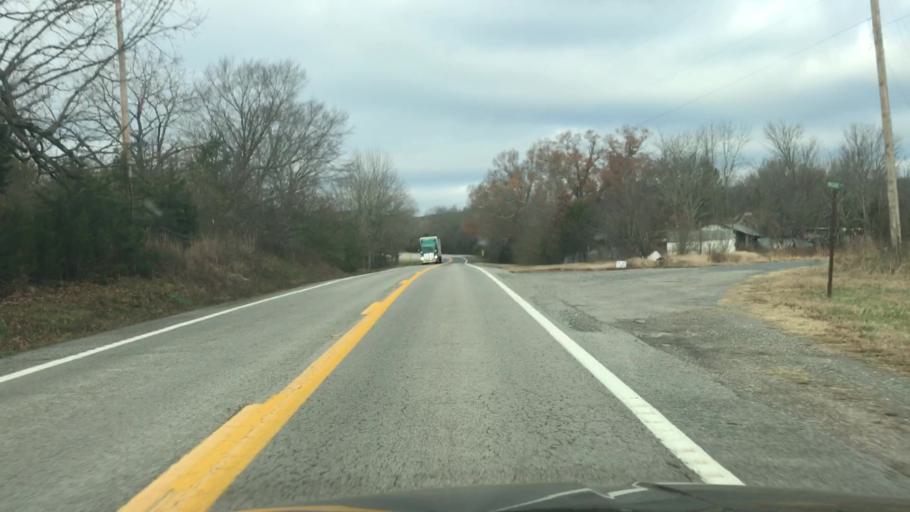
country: US
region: Arkansas
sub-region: Montgomery County
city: Mount Ida
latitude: 34.6571
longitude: -93.7604
